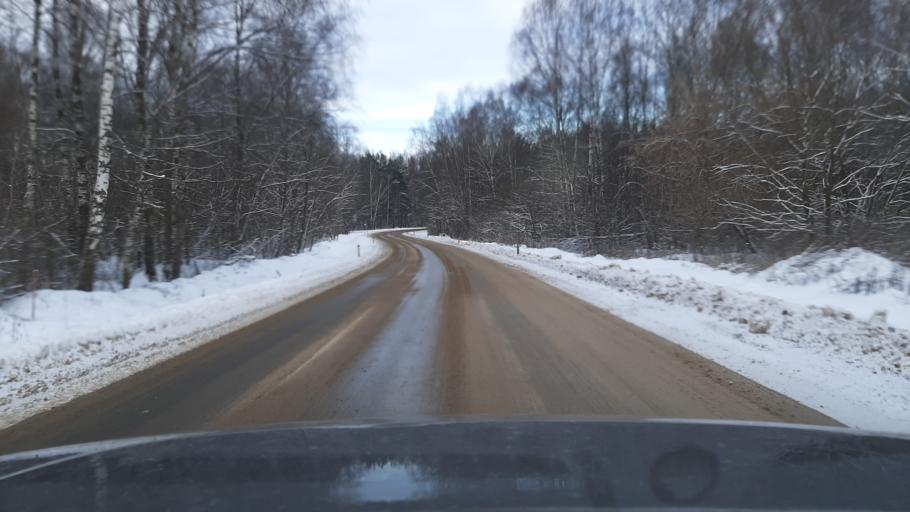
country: RU
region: Kostroma
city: Nerekhta
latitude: 57.4687
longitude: 40.6213
